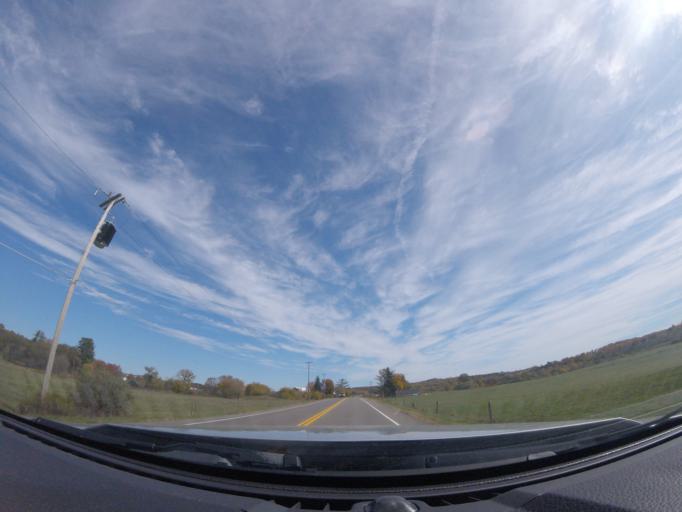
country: US
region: New York
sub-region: Tompkins County
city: Dryden
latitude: 42.5169
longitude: -76.3421
